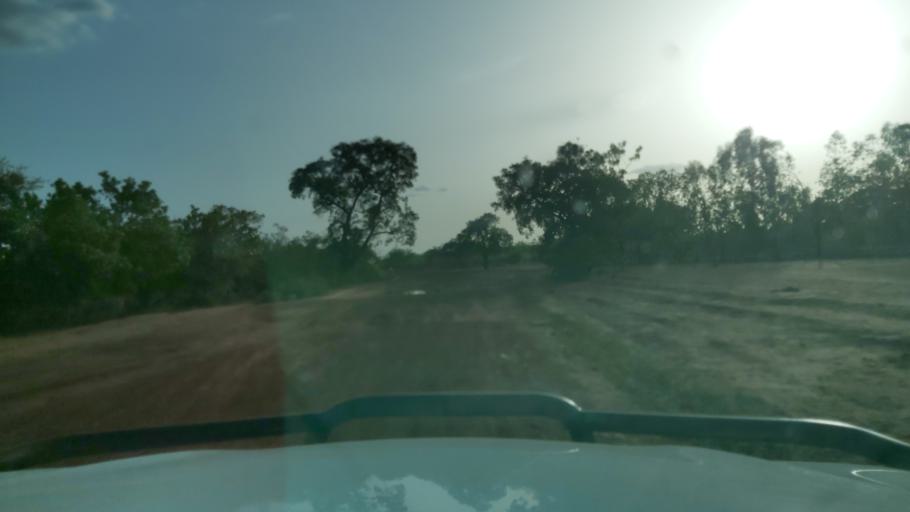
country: ML
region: Koulikoro
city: Kolokani
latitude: 13.2048
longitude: -7.9221
